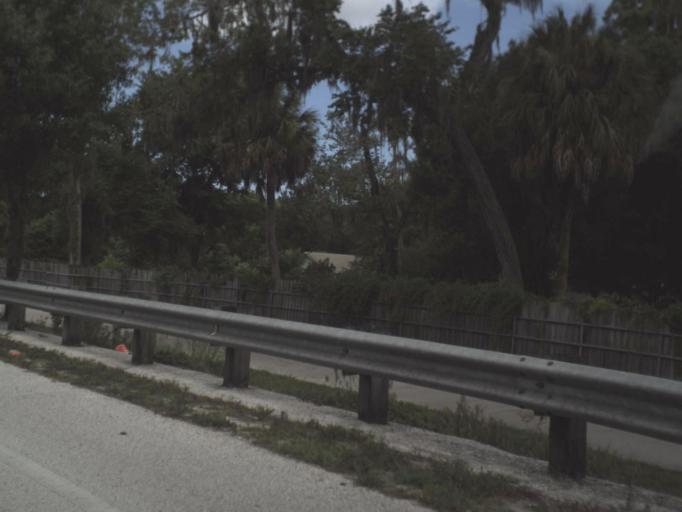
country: US
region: Florida
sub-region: Pinellas County
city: East Lake
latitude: 28.0920
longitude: -82.6977
